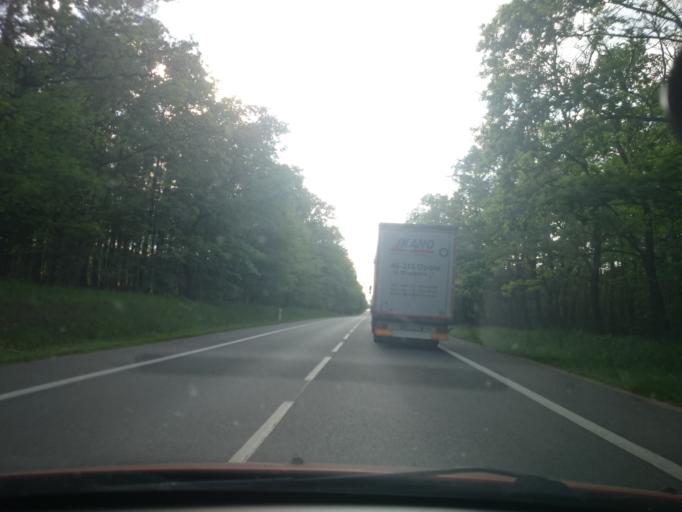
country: PL
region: Opole Voivodeship
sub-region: Powiat opolski
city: Chrzastowice
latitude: 50.6247
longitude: 18.0453
